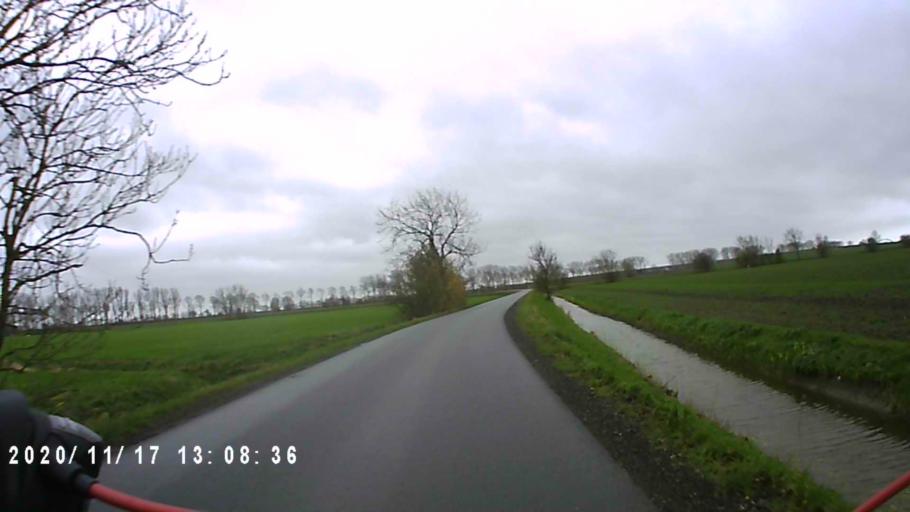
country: NL
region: Groningen
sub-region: Gemeente Zuidhorn
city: Zuidhorn
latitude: 53.2623
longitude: 6.4253
